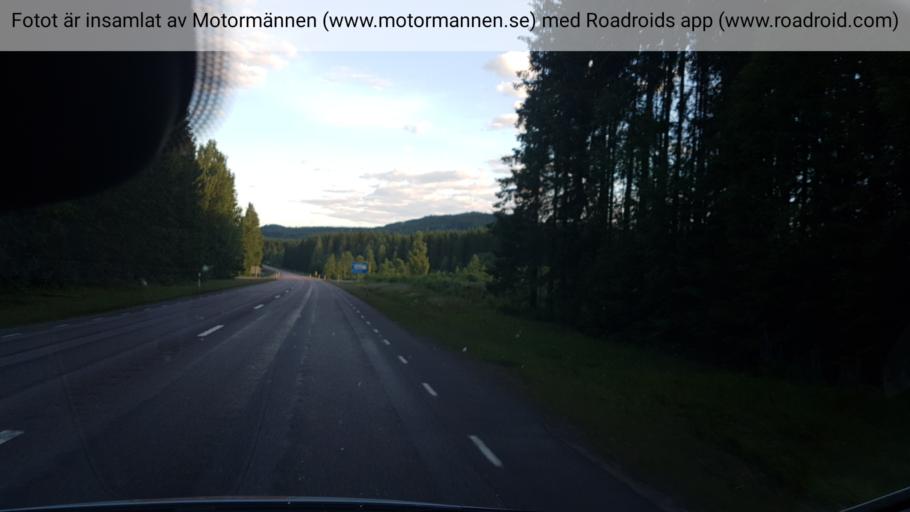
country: SE
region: Vaermland
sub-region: Torsby Kommun
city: Torsby
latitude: 60.0954
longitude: 13.0234
